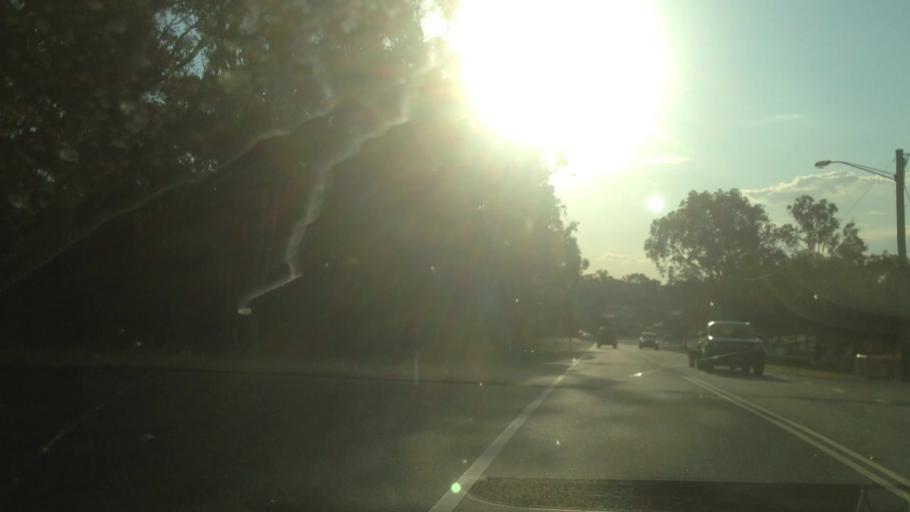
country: AU
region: New South Wales
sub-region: Cessnock
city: Kurri Kurri
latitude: -32.8280
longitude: 151.4911
